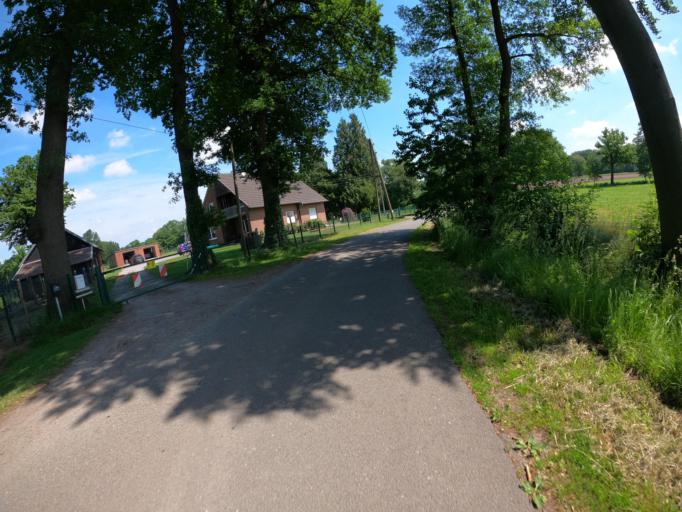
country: DE
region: North Rhine-Westphalia
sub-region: Regierungsbezirk Dusseldorf
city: Hunxe
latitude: 51.6964
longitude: 6.8035
